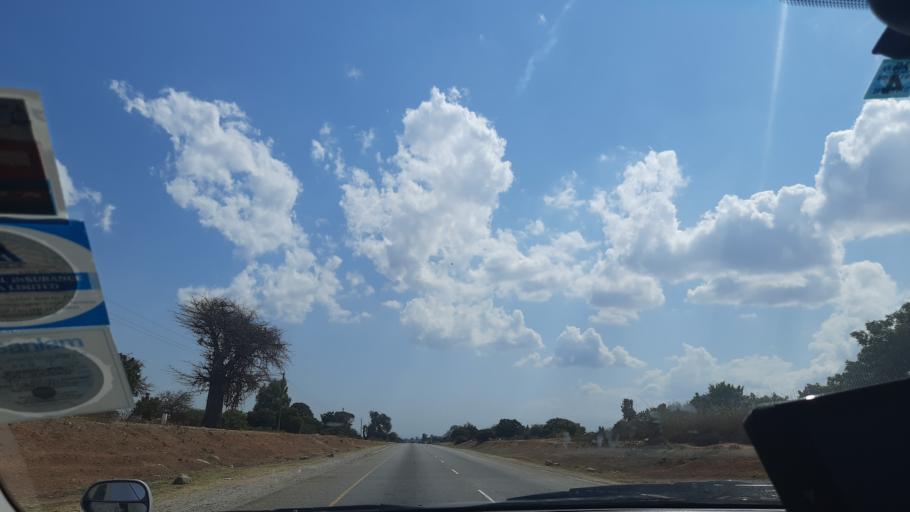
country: TZ
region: Singida
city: Kintinku
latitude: -6.0100
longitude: 35.4189
